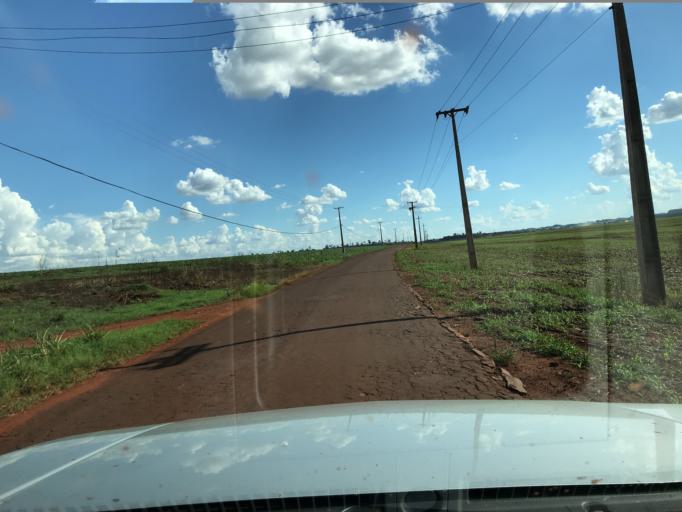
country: BR
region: Parana
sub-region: Palotina
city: Palotina
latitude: -24.2488
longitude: -53.7927
